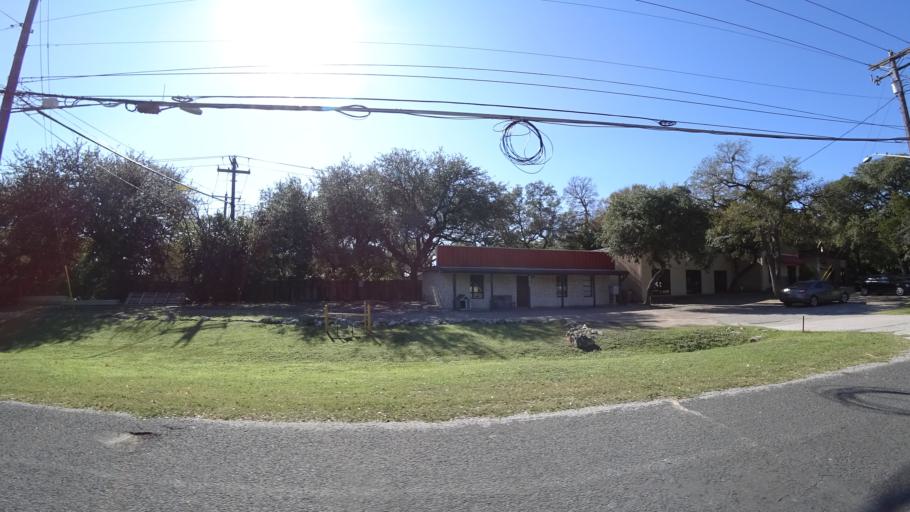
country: US
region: Texas
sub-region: Williamson County
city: Jollyville
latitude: 30.3816
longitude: -97.7435
